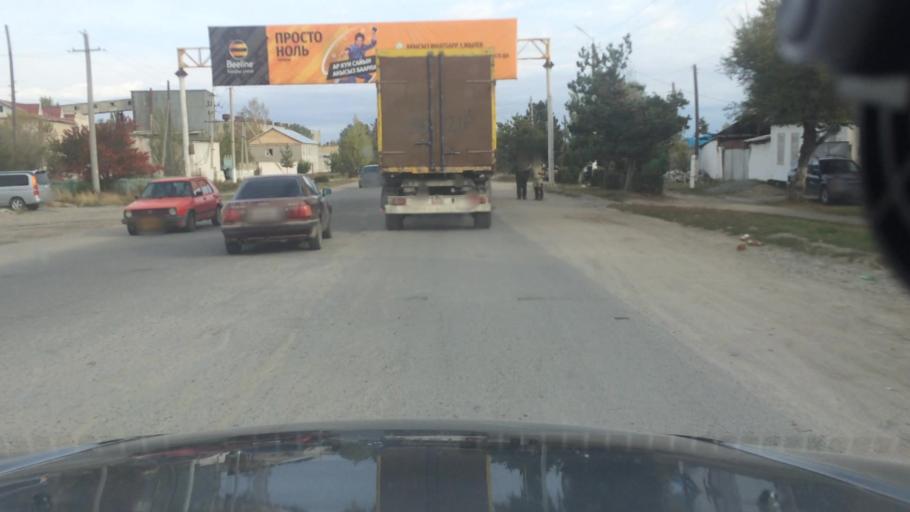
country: KG
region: Ysyk-Koel
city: Karakol
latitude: 42.5133
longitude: 78.3858
